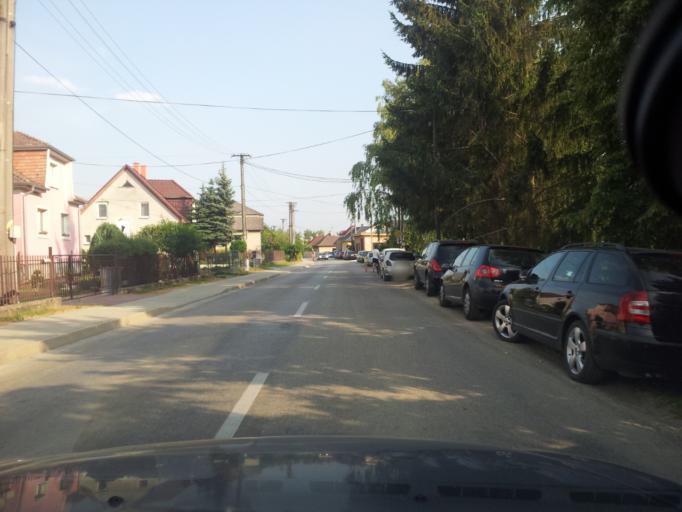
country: SK
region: Nitriansky
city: Banovce nad Bebravou
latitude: 48.7654
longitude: 18.2114
